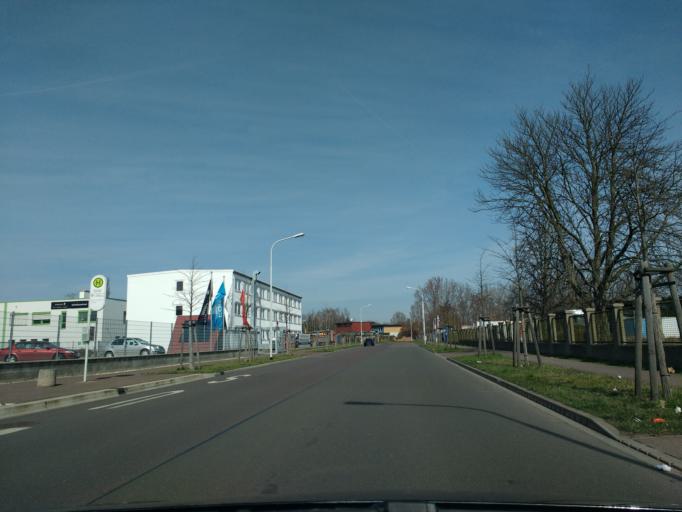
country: DE
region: Saxony-Anhalt
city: Halle (Saale)
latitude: 51.4862
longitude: 12.0115
